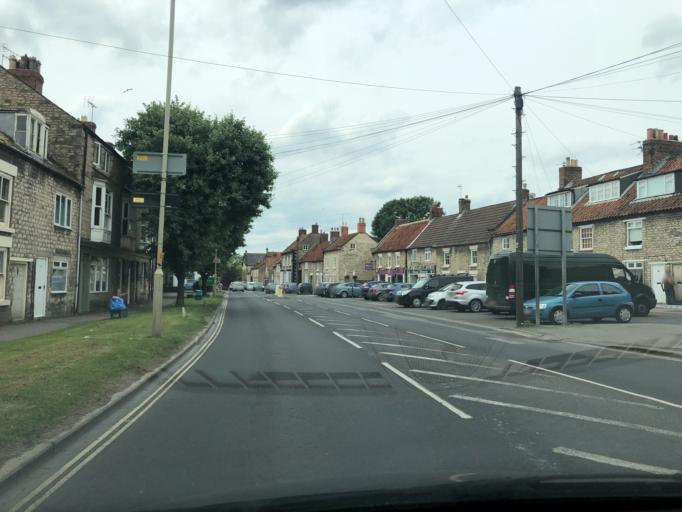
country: GB
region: England
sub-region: North Yorkshire
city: Pickering
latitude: 54.2443
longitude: -0.7758
